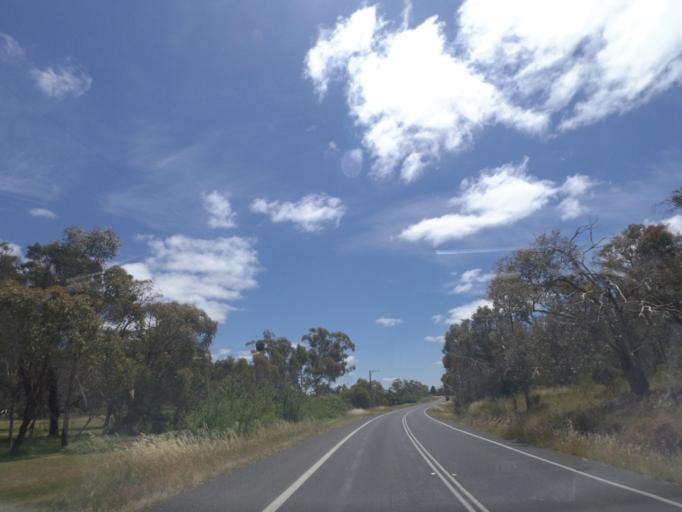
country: AU
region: Victoria
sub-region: Mount Alexander
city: Castlemaine
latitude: -37.2811
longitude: 144.1516
